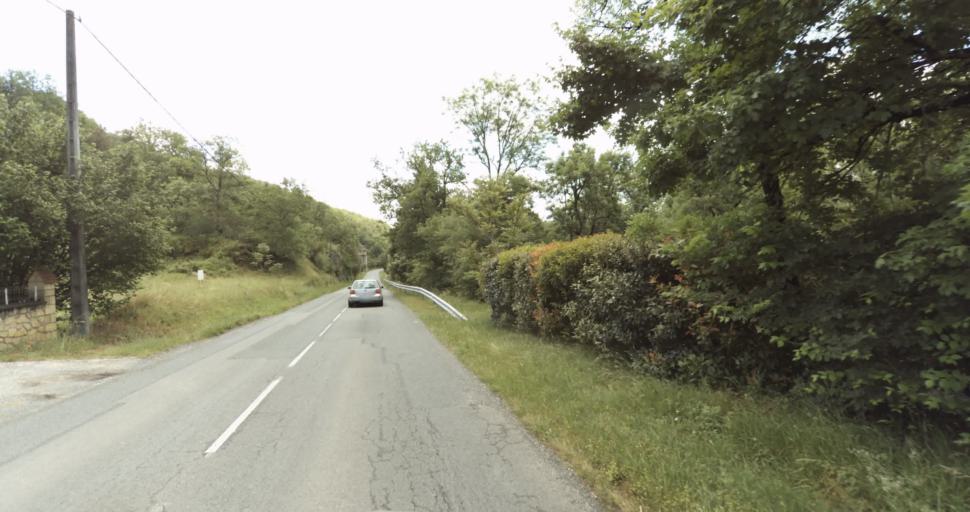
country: FR
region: Aquitaine
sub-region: Departement de la Dordogne
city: Lalinde
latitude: 44.8191
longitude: 0.7084
